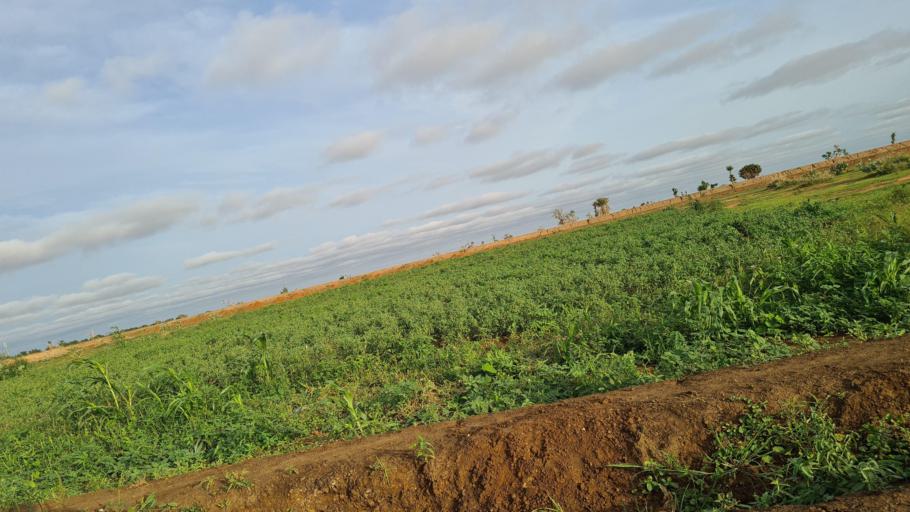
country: NE
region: Tahoua
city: Birni N Konni
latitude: 13.7874
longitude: 5.2325
